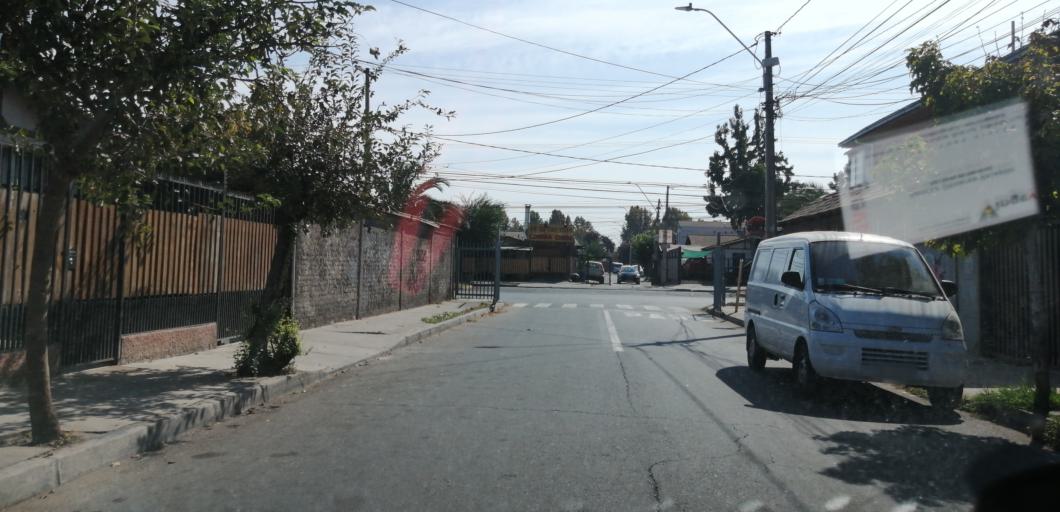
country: CL
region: Santiago Metropolitan
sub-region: Provincia de Santiago
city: Lo Prado
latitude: -33.4567
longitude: -70.7493
